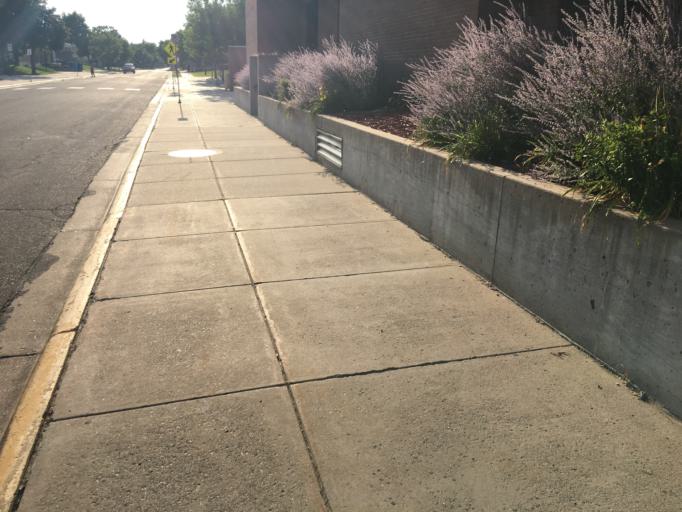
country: US
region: Minnesota
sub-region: Stearns County
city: Saint Cloud
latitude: 45.5538
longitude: -94.1494
